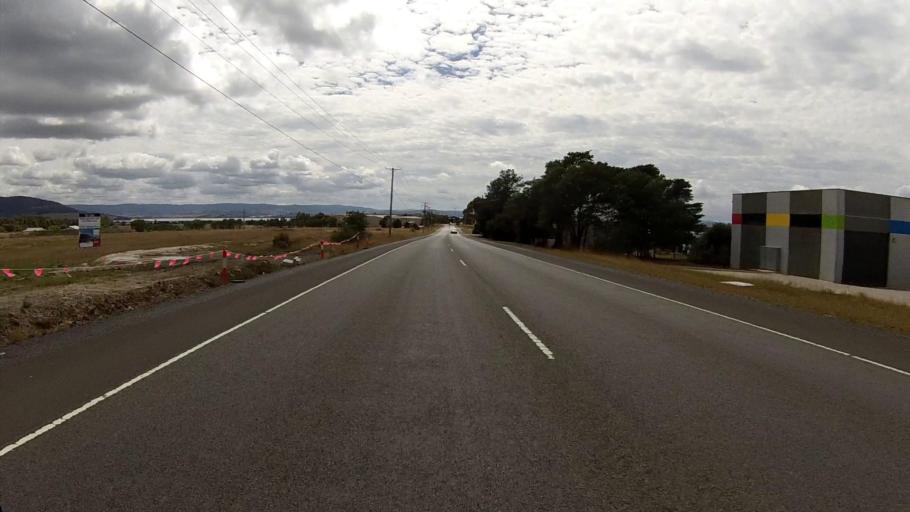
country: AU
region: Tasmania
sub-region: Clarence
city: Cambridge
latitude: -42.8328
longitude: 147.4590
